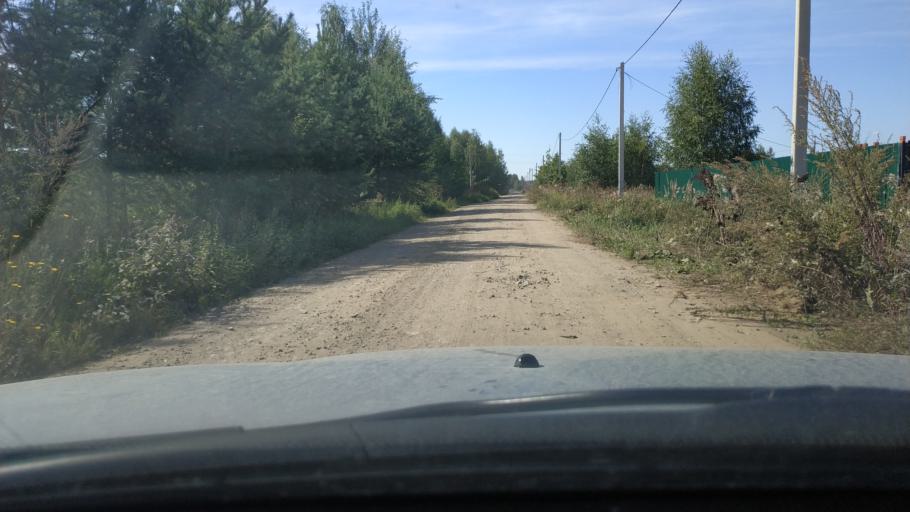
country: RU
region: Kostroma
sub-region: Kostromskoy Rayon
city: Kostroma
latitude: 57.7790
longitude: 40.7469
